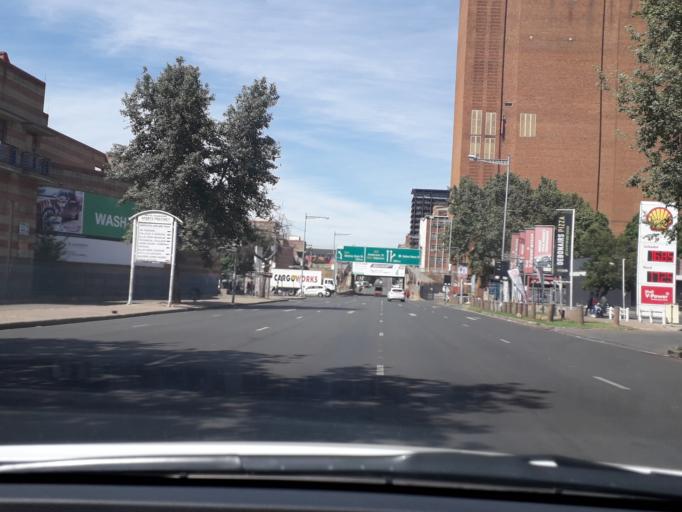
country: ZA
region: Gauteng
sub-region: City of Johannesburg Metropolitan Municipality
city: Johannesburg
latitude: -26.1958
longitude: 28.0582
